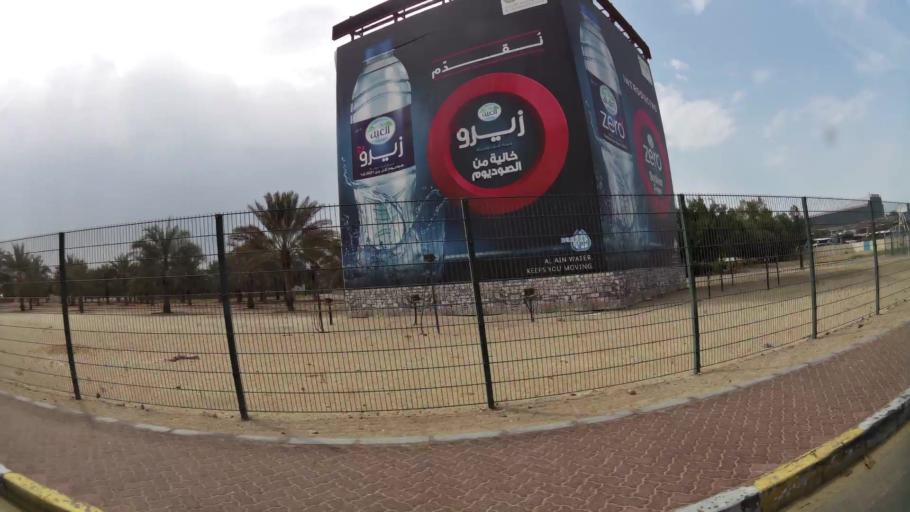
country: AE
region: Abu Dhabi
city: Abu Dhabi
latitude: 24.4285
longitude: 54.4695
